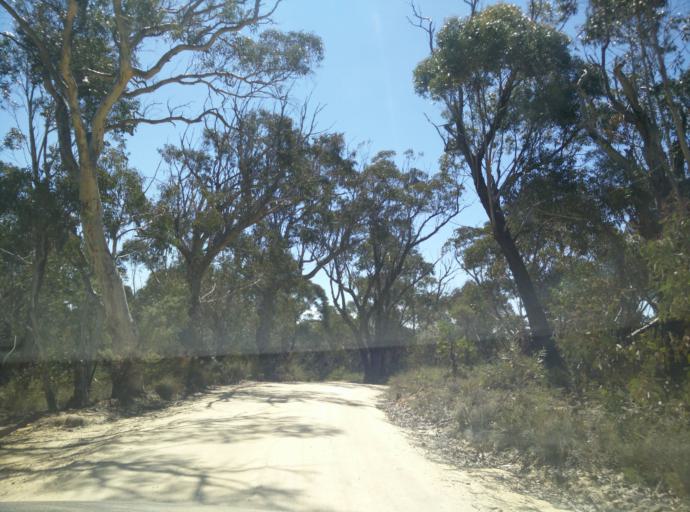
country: AU
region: New South Wales
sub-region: Blue Mountains Municipality
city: Blackheath
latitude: -33.5694
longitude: 150.2791
